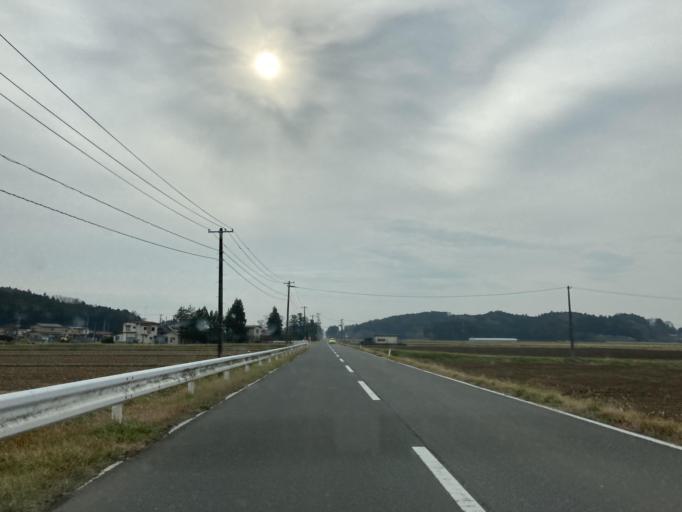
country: JP
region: Miyagi
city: Wakuya
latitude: 38.7022
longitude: 141.2738
